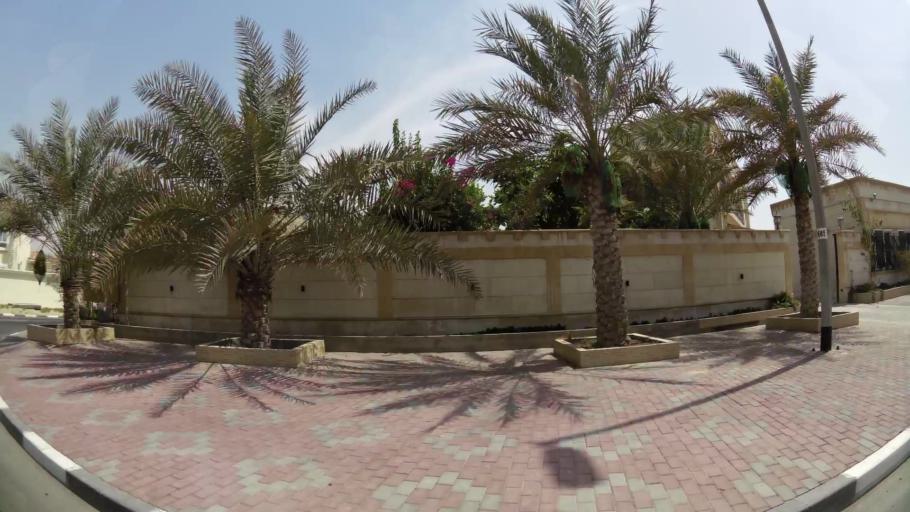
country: AE
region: Ash Shariqah
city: Sharjah
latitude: 25.2423
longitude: 55.4269
